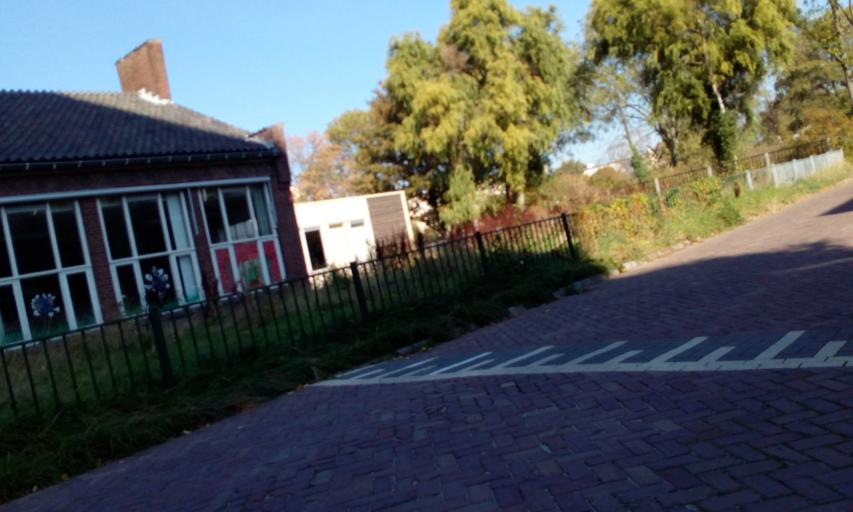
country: NL
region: South Holland
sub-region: Gemeente Vlaardingen
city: Vlaardingen
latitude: 51.9185
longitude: 4.3596
